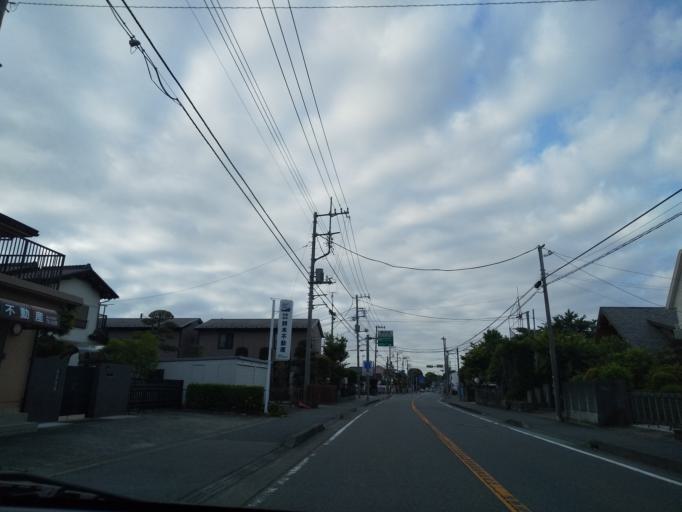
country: JP
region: Kanagawa
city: Zama
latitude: 35.5300
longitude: 139.3733
